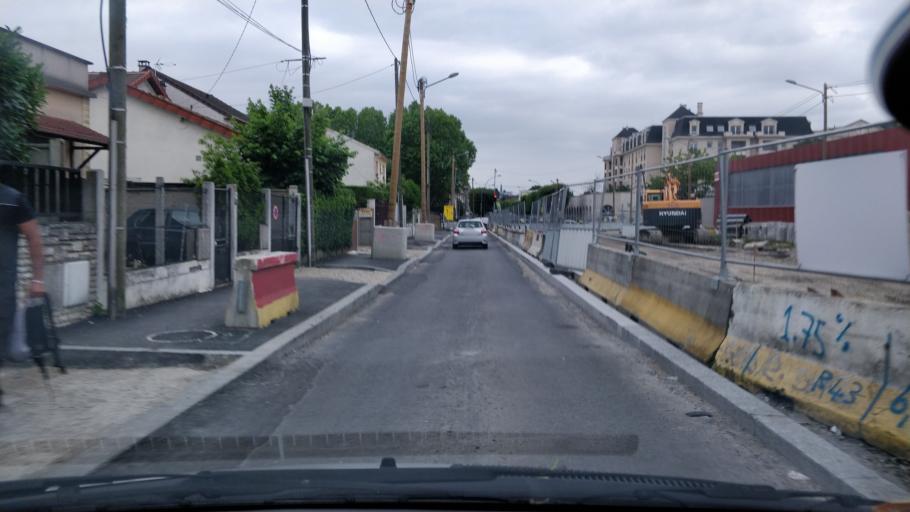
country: FR
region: Ile-de-France
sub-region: Departement de Seine-Saint-Denis
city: Le Raincy
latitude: 48.9068
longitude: 2.5243
